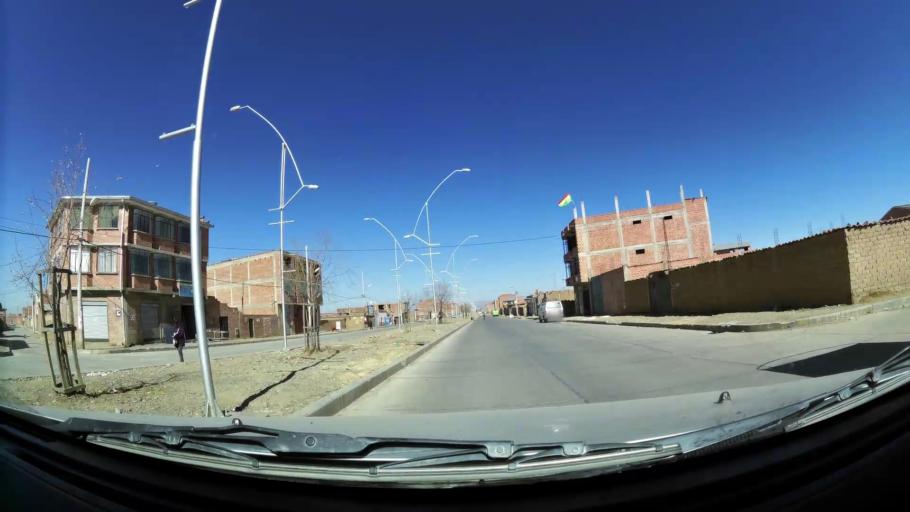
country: BO
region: La Paz
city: La Paz
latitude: -16.5329
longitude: -68.2250
